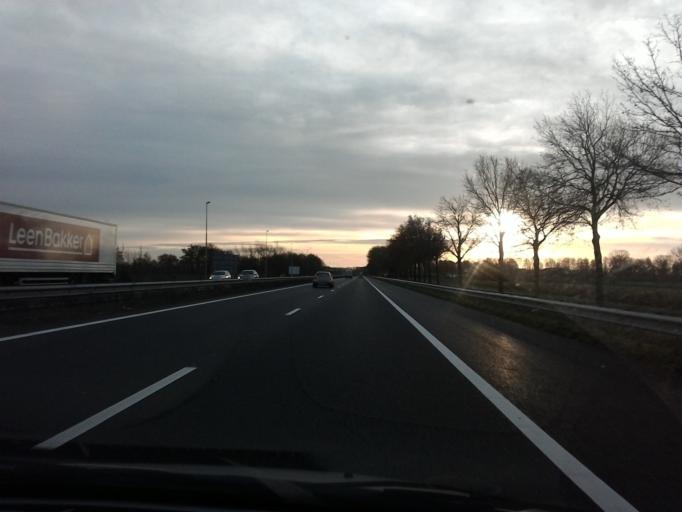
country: NL
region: North Brabant
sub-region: Gemeente Heeze-Leende
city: Heeze
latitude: 51.3414
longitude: 5.5594
